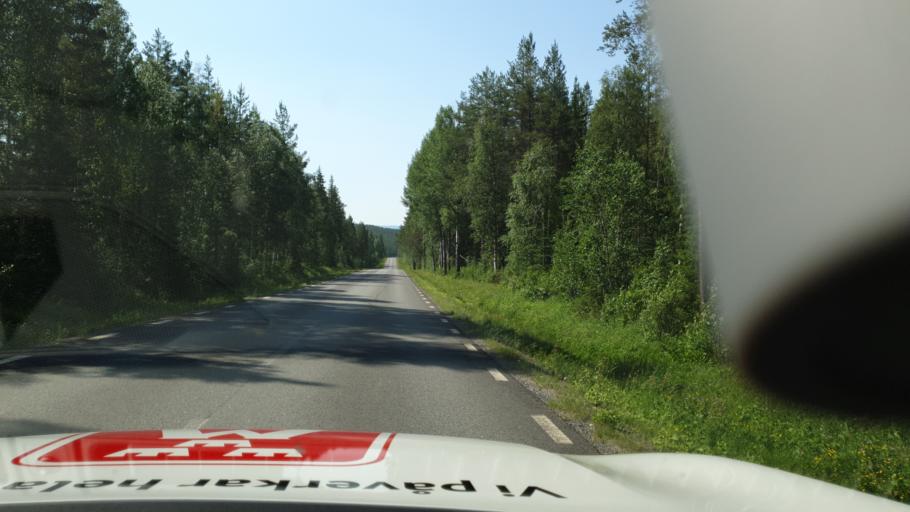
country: SE
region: Vaesterbotten
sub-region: Skelleftea Kommun
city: Langsele
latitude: 64.9615
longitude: 20.0432
